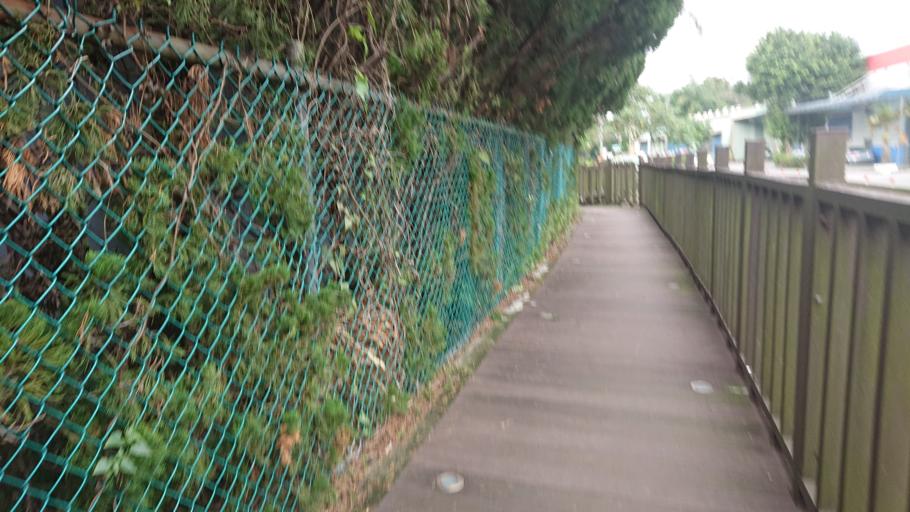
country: TW
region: Taipei
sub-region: Taipei
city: Banqiao
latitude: 24.9607
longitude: 121.4436
